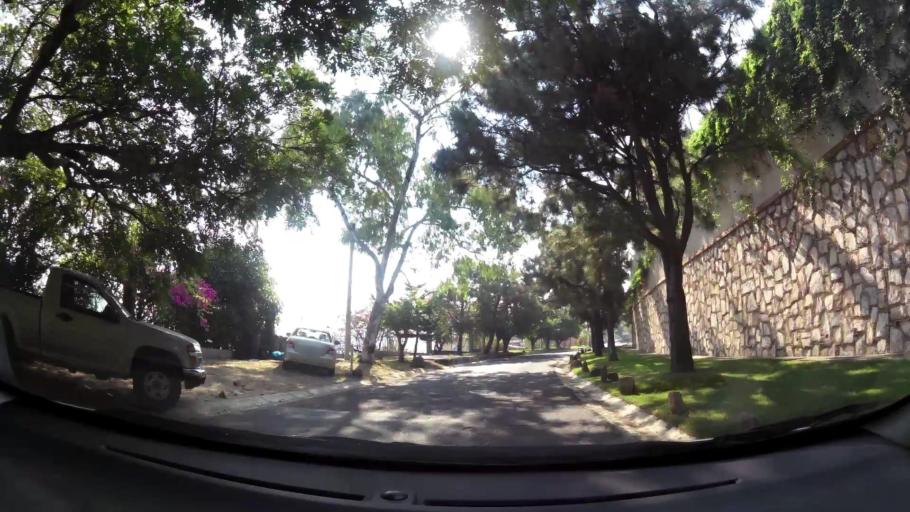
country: SV
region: La Libertad
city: Antiguo Cuscatlan
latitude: 13.6812
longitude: -89.2305
